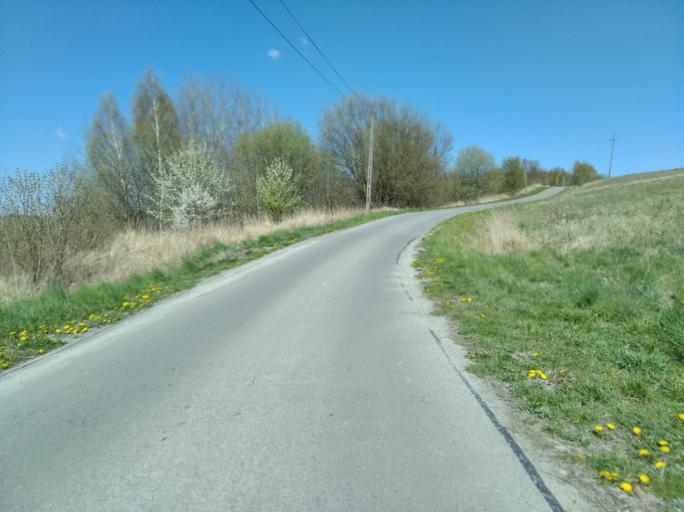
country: PL
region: Subcarpathian Voivodeship
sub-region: Powiat strzyzowski
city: Wisniowa
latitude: 49.9154
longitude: 21.6760
